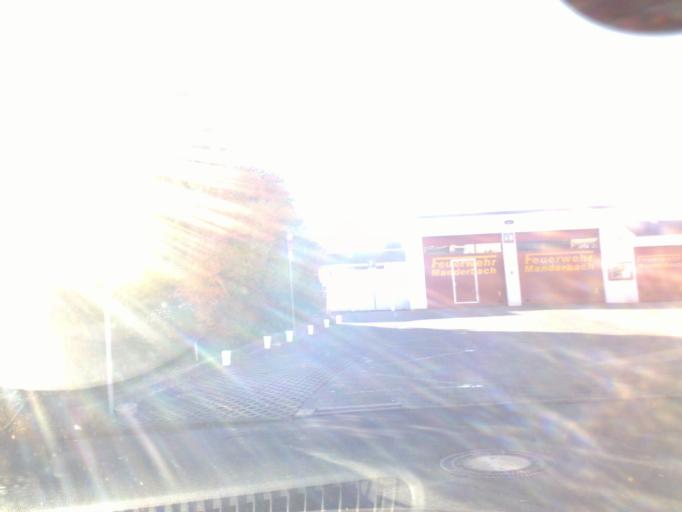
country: DE
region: Hesse
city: Dillenburg
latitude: 50.7663
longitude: 8.2647
